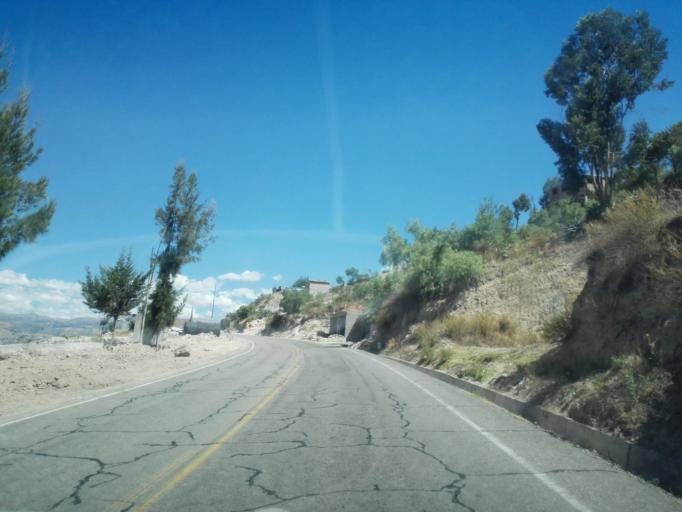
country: PE
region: Ayacucho
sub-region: Provincia de Huamanga
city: Ayacucho
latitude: -13.1656
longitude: -74.2427
